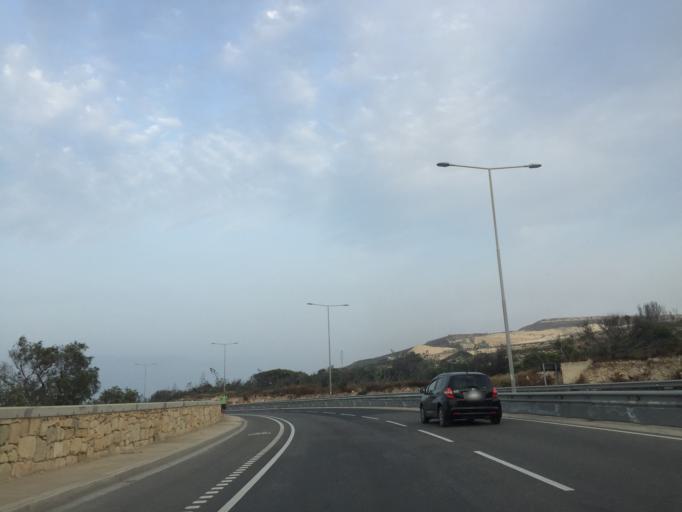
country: MT
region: Saint Paul's Bay
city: San Pawl il-Bahar
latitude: 35.9529
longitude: 14.4359
